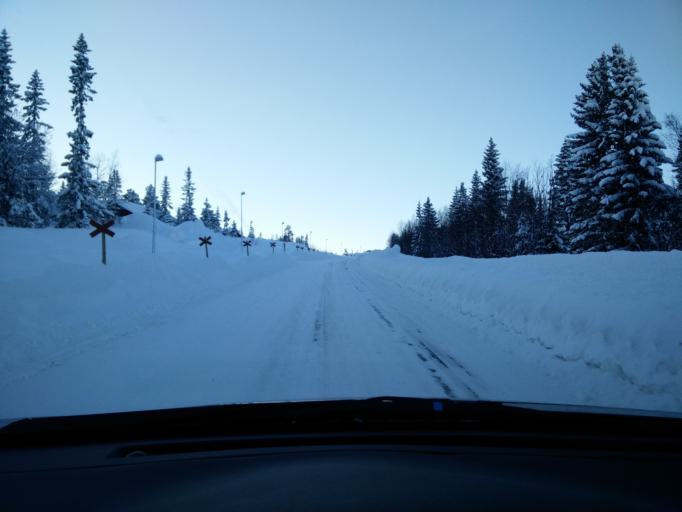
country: SE
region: Jaemtland
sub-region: Bergs Kommun
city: Hoverberg
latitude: 62.5020
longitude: 14.1037
